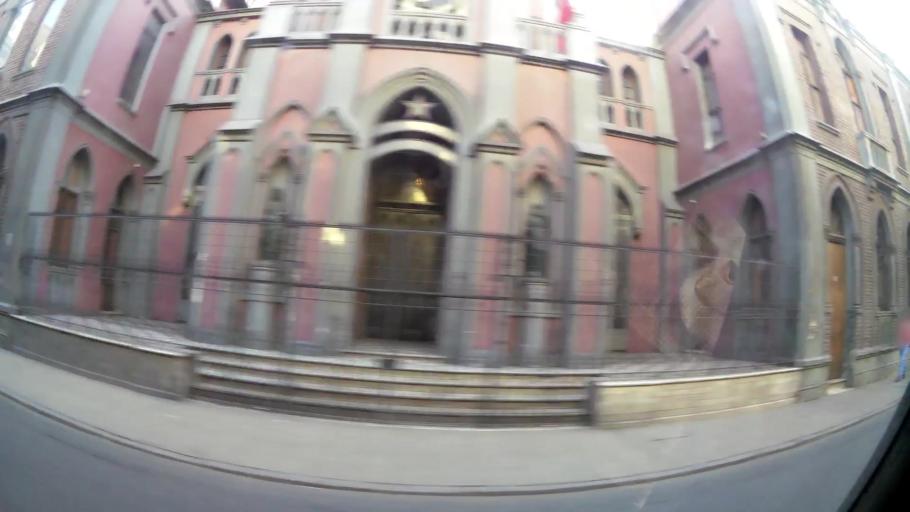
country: CL
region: Santiago Metropolitan
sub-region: Provincia de Santiago
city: Santiago
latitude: -33.4351
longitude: -70.6475
